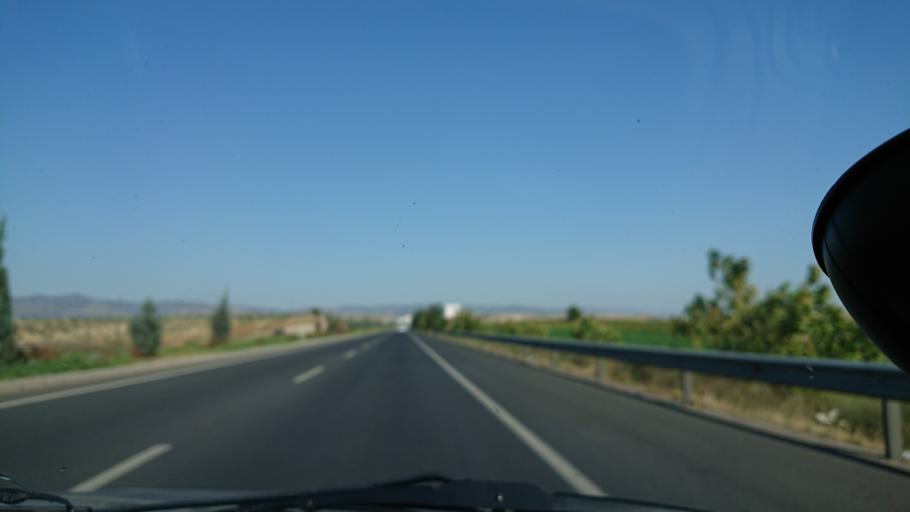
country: TR
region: Manisa
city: Adala
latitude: 38.5092
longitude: 28.2847
